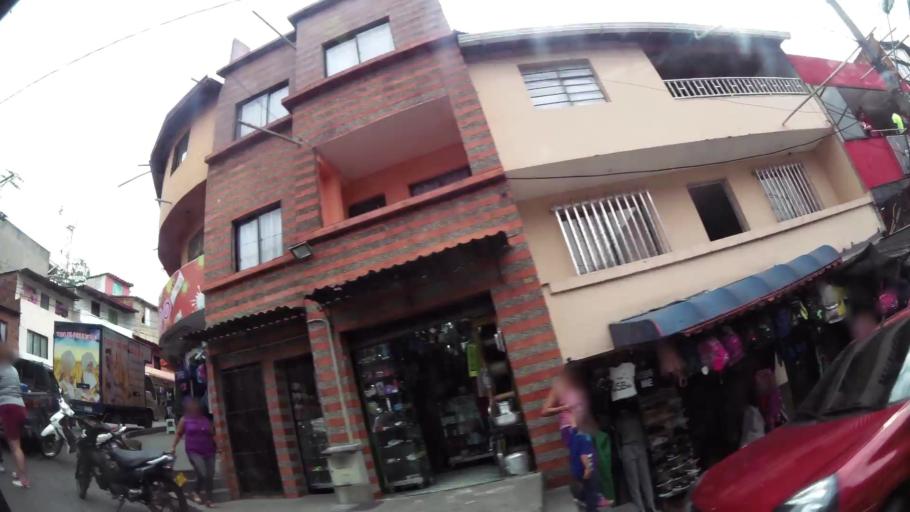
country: CO
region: Antioquia
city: Bello
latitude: 6.3062
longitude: -75.5530
